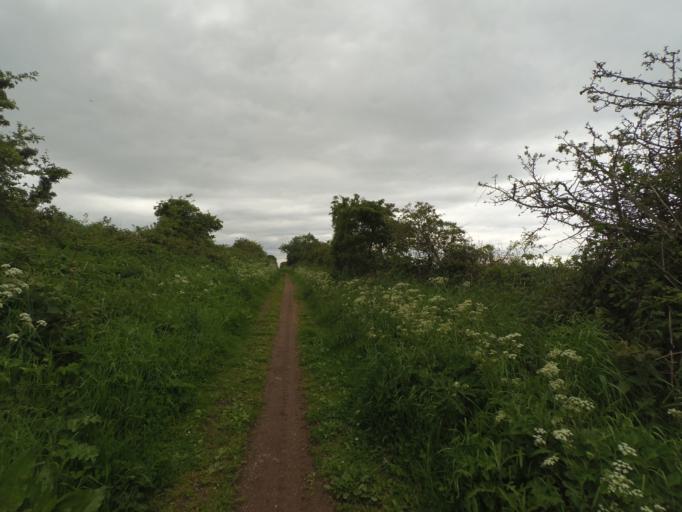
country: GB
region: Scotland
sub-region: East Lothian
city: Prestonpans
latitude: 55.9257
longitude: -2.9917
